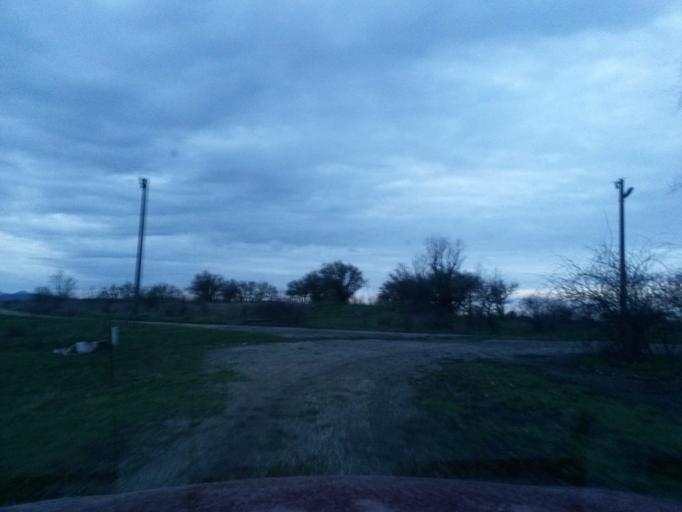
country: HU
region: Borsod-Abauj-Zemplen
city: Karcsa
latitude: 48.4176
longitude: 21.8723
